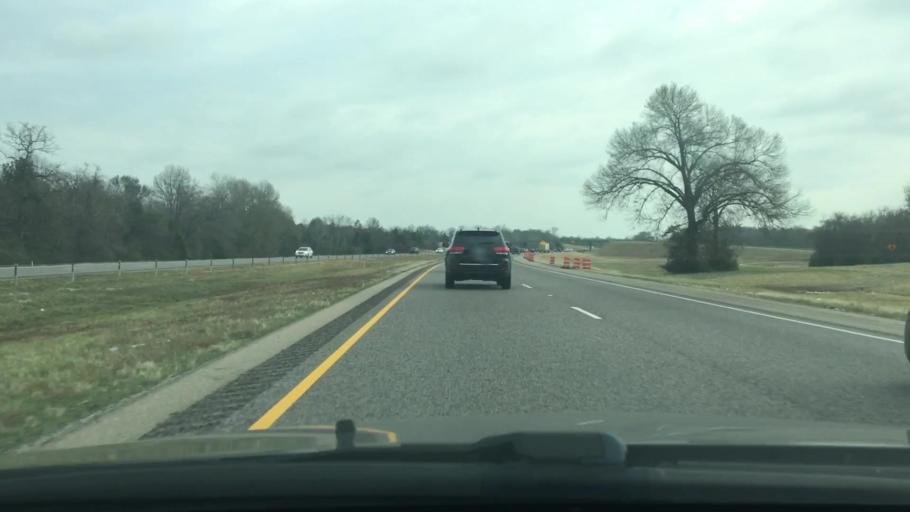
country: US
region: Texas
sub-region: Leon County
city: Buffalo
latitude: 31.5045
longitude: -96.0993
